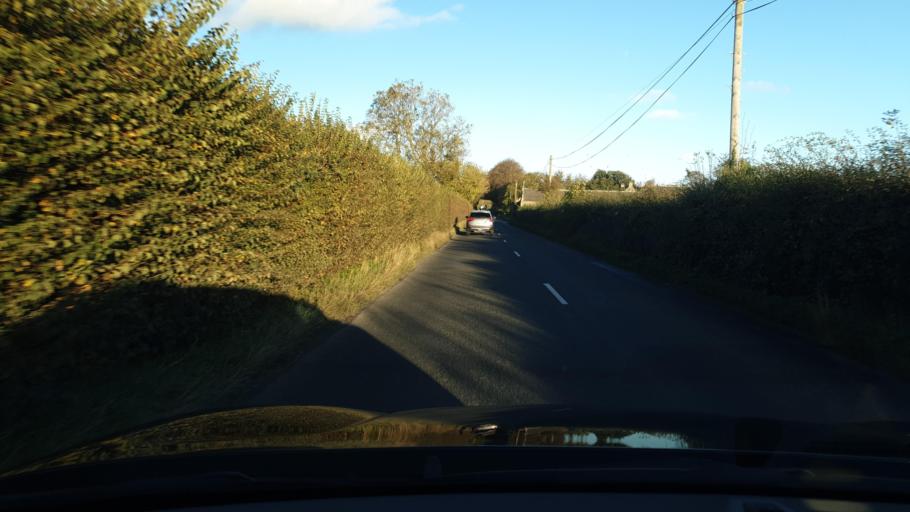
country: IE
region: Leinster
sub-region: Lu
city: Drogheda
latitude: 53.6950
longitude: -6.3299
